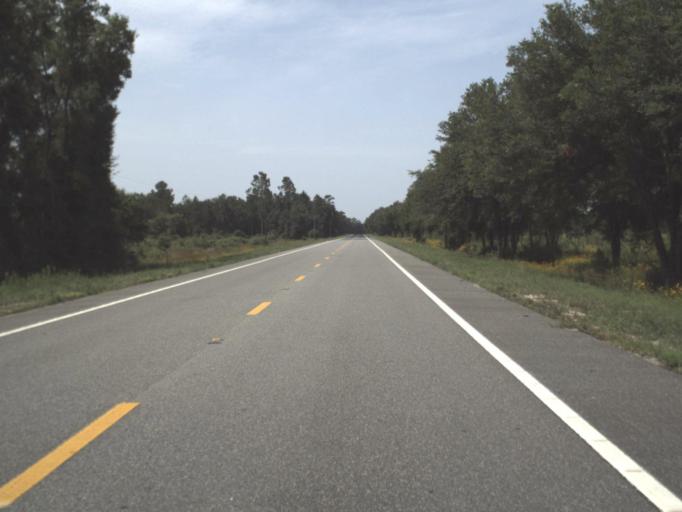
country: US
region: Florida
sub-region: Taylor County
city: Steinhatchee
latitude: 29.7940
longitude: -83.3209
